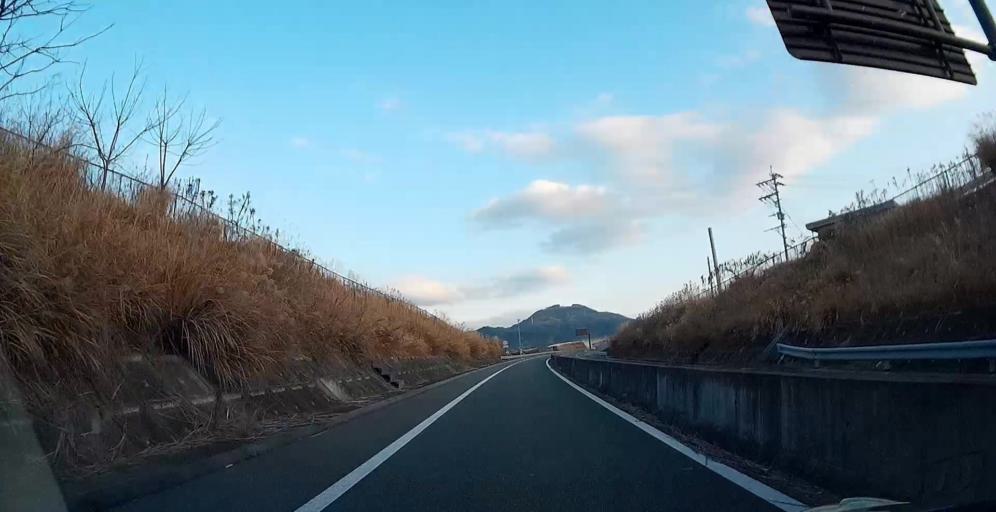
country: JP
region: Kumamoto
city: Kumamoto
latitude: 32.7535
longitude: 130.7933
